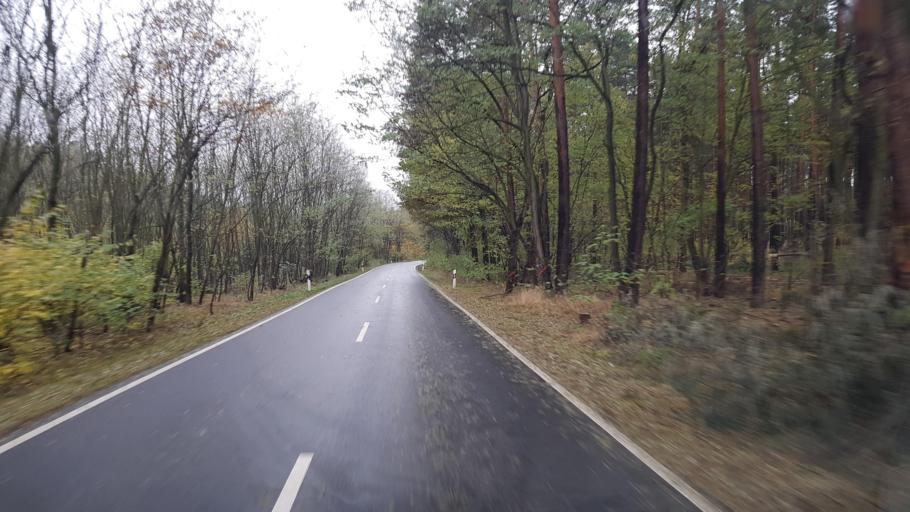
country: DE
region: Brandenburg
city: Drebkau
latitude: 51.6644
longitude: 14.2732
